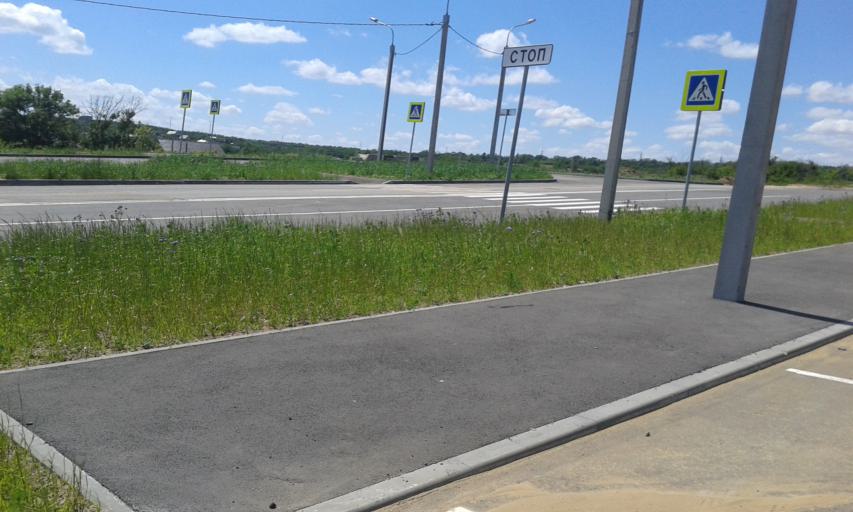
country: RU
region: Volgograd
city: Volgograd
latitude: 48.6600
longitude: 44.4042
